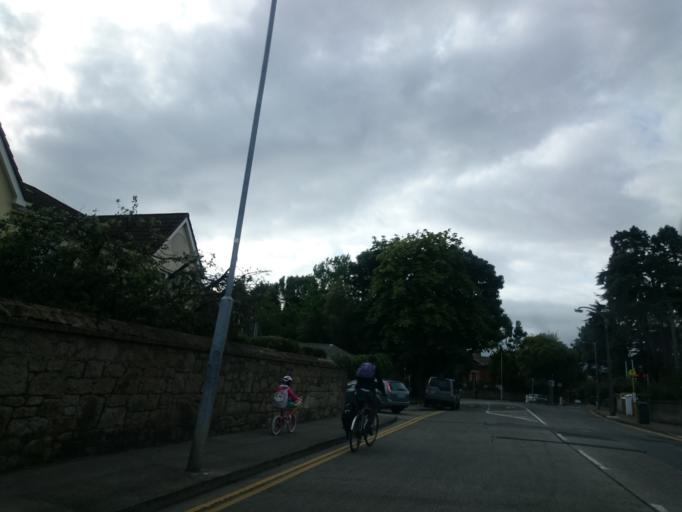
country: IE
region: Leinster
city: Rathgar
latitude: 53.3106
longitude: -6.2737
